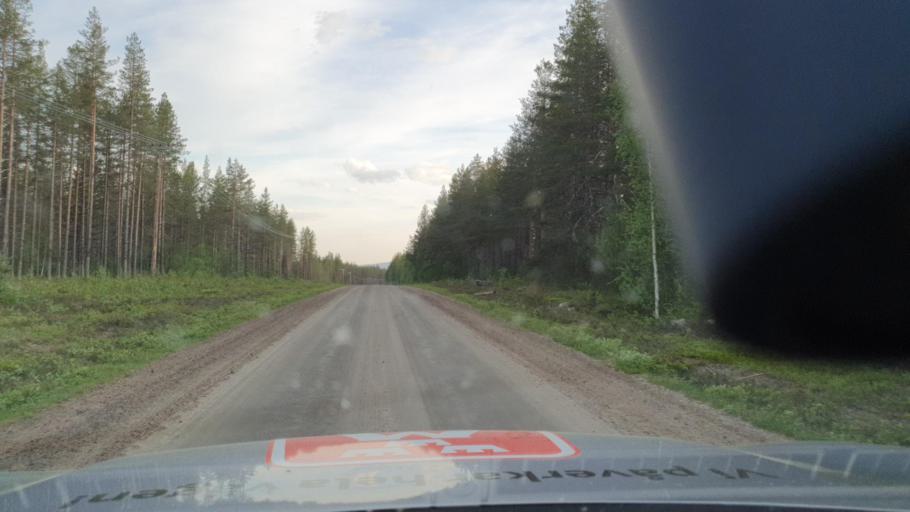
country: SE
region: Norrbotten
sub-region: Bodens Kommun
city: Boden
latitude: 66.3436
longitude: 21.4432
